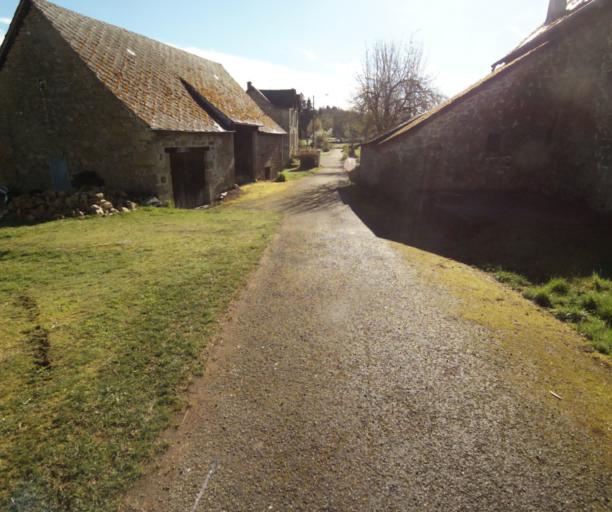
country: FR
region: Limousin
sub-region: Departement de la Correze
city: Laguenne
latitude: 45.2670
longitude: 1.8553
